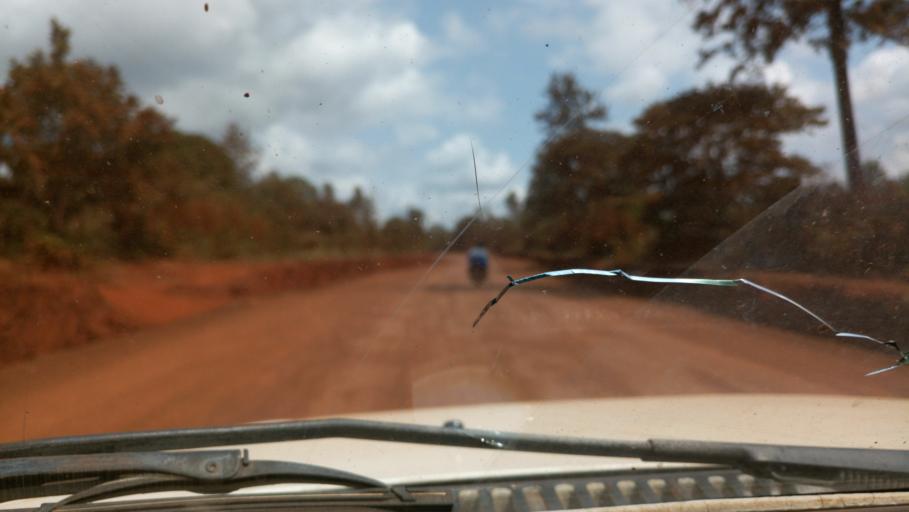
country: KE
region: Murang'a District
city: Karuri
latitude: -0.7447
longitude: 37.1864
